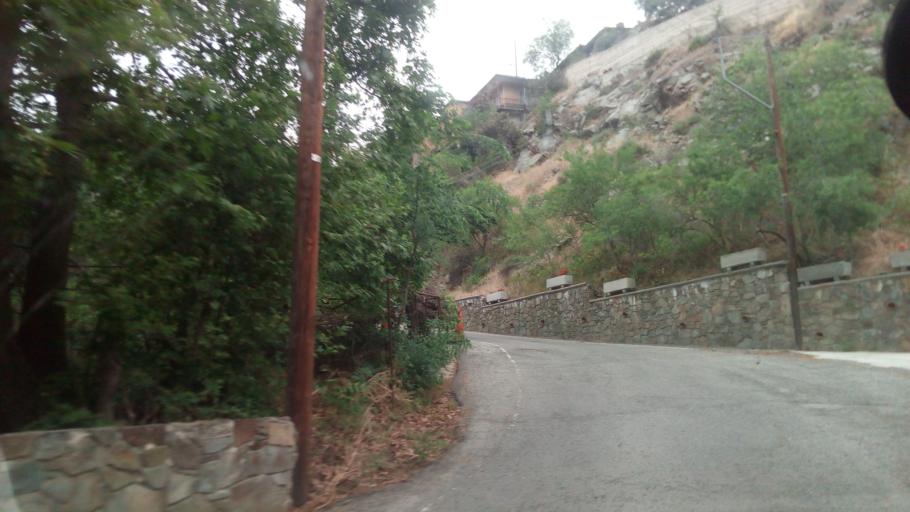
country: CY
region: Lefkosia
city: Kakopetria
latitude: 34.9611
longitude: 32.7503
